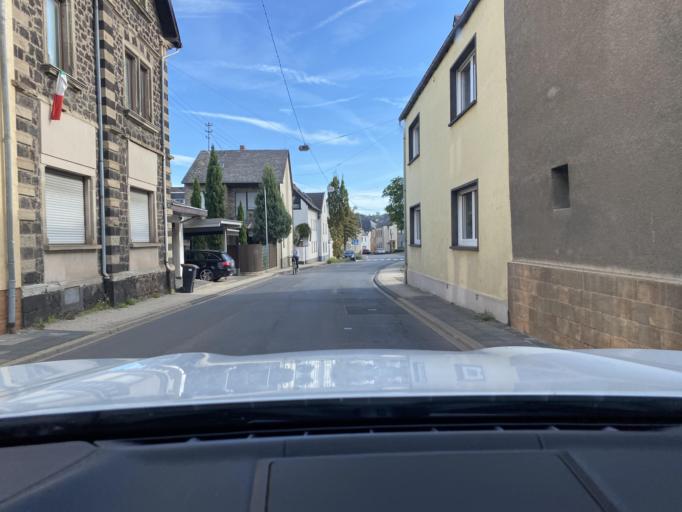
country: DE
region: Rheinland-Pfalz
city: Saffig
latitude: 50.4024
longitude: 7.4105
